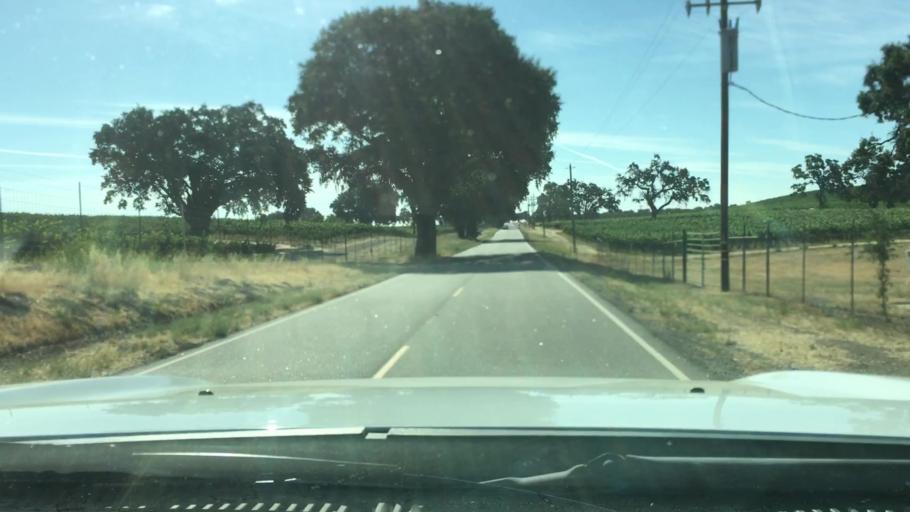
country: US
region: California
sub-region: San Luis Obispo County
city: Atascadero
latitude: 35.5542
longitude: -120.6179
